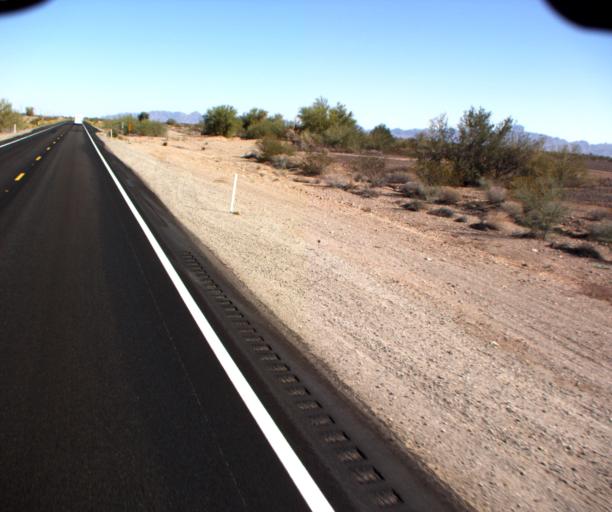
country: US
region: Arizona
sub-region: Yuma County
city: Wellton
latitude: 32.9705
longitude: -114.2908
